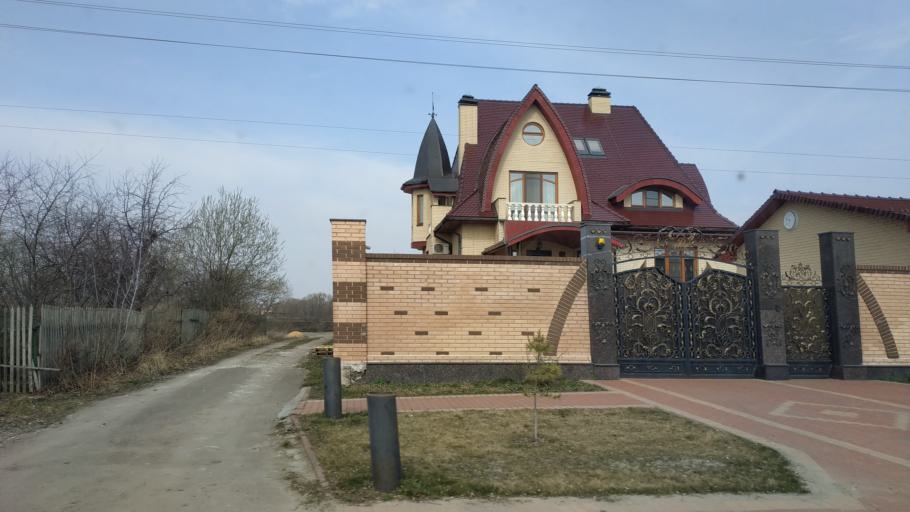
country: RU
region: Moskovskaya
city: Malyshevo
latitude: 55.4014
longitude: 38.3662
